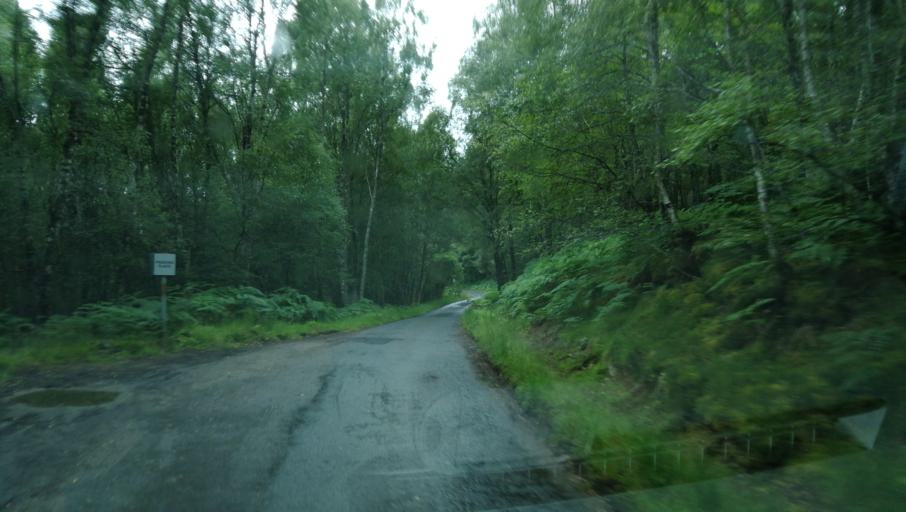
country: GB
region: Scotland
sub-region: Highland
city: Spean Bridge
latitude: 57.2774
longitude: -4.9443
